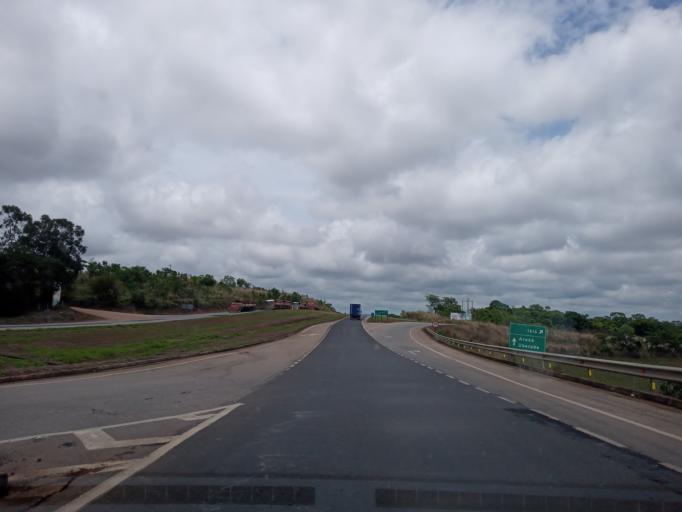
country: BR
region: Minas Gerais
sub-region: Ibia
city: Ibia
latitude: -19.5902
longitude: -46.4948
